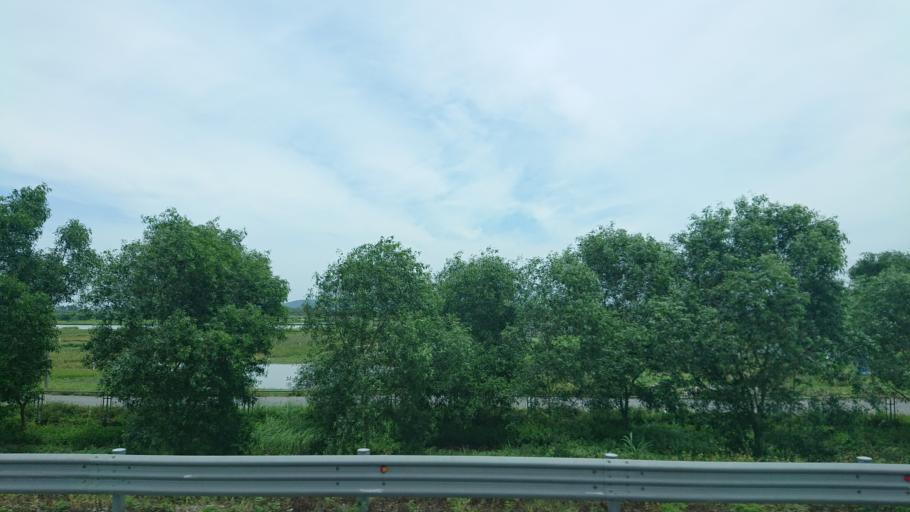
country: VN
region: Hai Phong
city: Tien Lang
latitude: 20.7710
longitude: 106.5904
